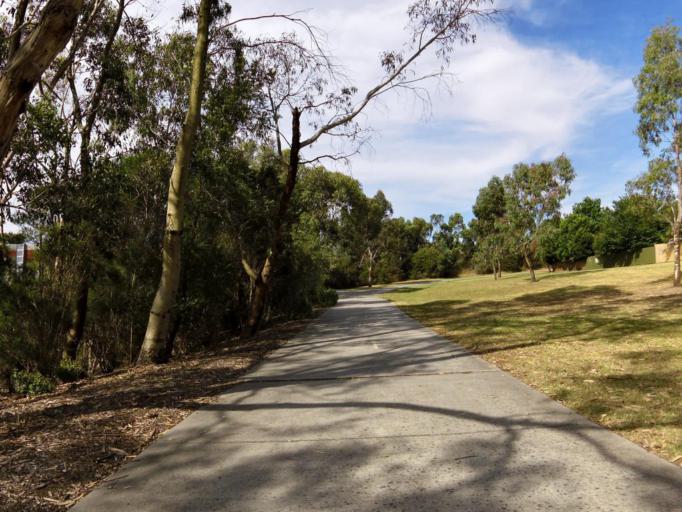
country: AU
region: Victoria
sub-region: Casey
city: Eumemmerring
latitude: -37.9966
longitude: 145.2663
